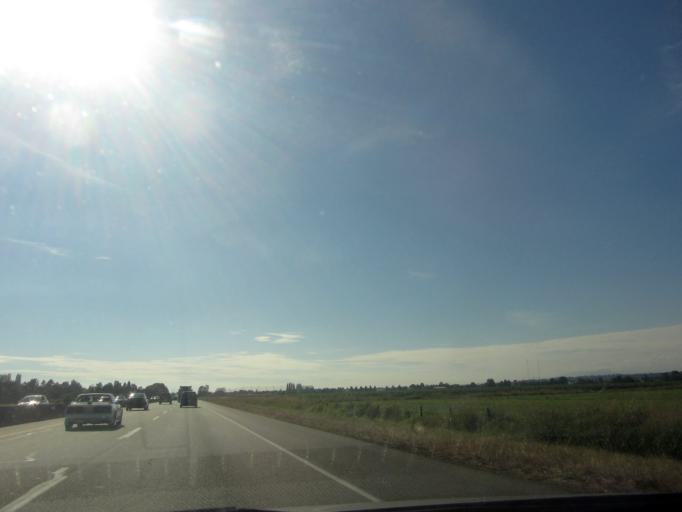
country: CA
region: British Columbia
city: Richmond
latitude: 49.1775
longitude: -123.0496
